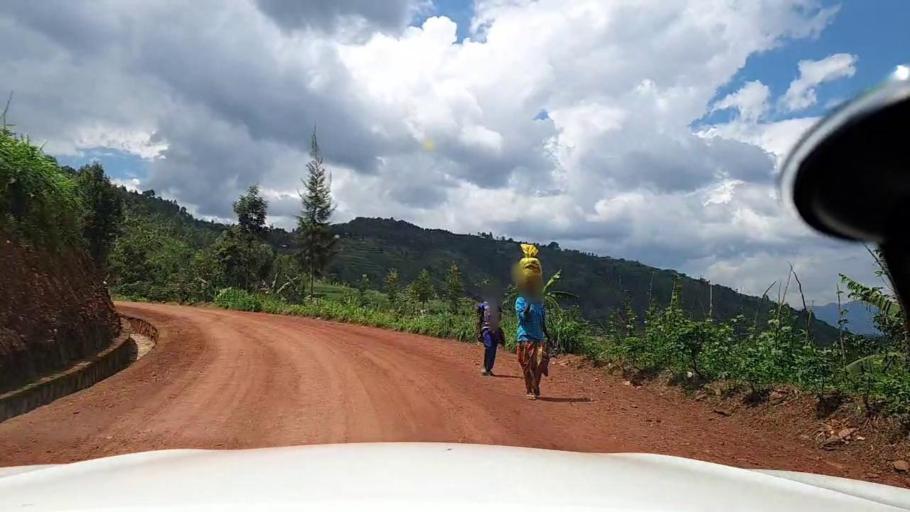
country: RW
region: Northern Province
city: Byumba
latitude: -1.7541
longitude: 29.8484
